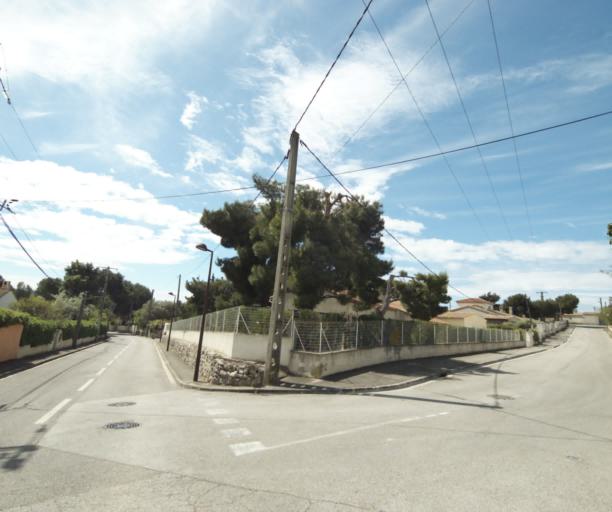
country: FR
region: Provence-Alpes-Cote d'Azur
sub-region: Departement des Bouches-du-Rhone
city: Rognac
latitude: 43.5152
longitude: 5.2195
